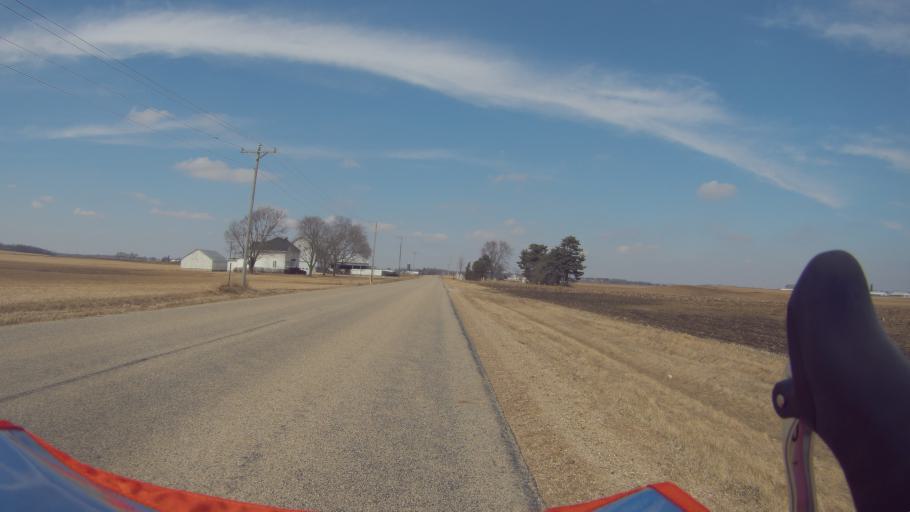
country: US
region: Wisconsin
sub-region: Dane County
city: Waunakee
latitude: 43.1684
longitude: -89.4967
